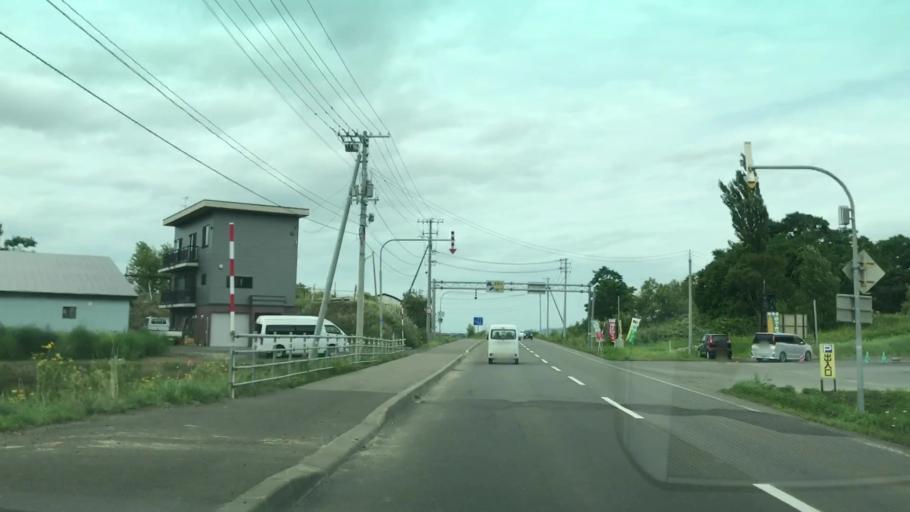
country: JP
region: Hokkaido
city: Iwanai
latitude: 42.9780
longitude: 140.6285
